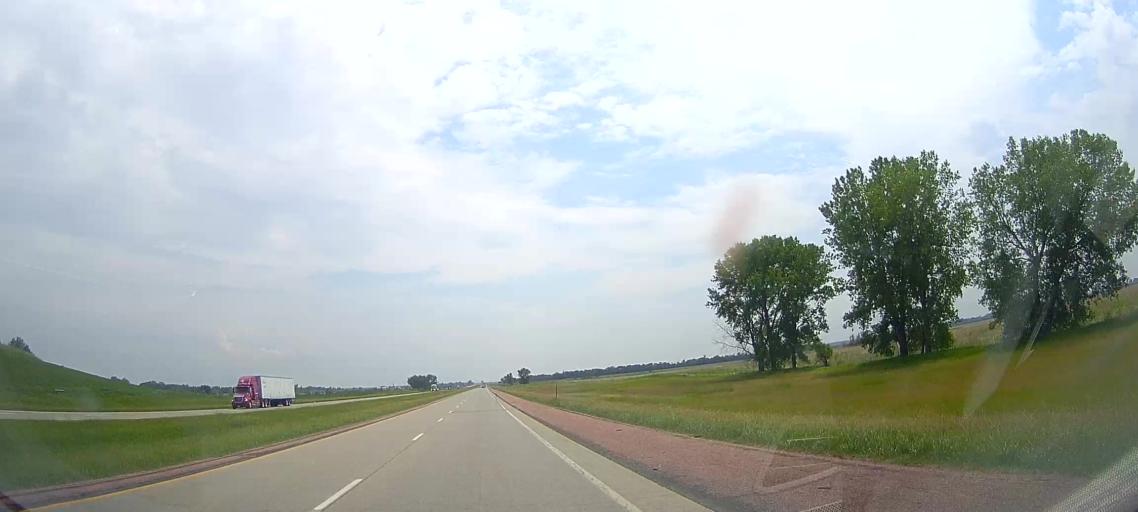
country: US
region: South Dakota
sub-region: Clay County
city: Vermillion
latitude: 42.8937
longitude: -96.7954
